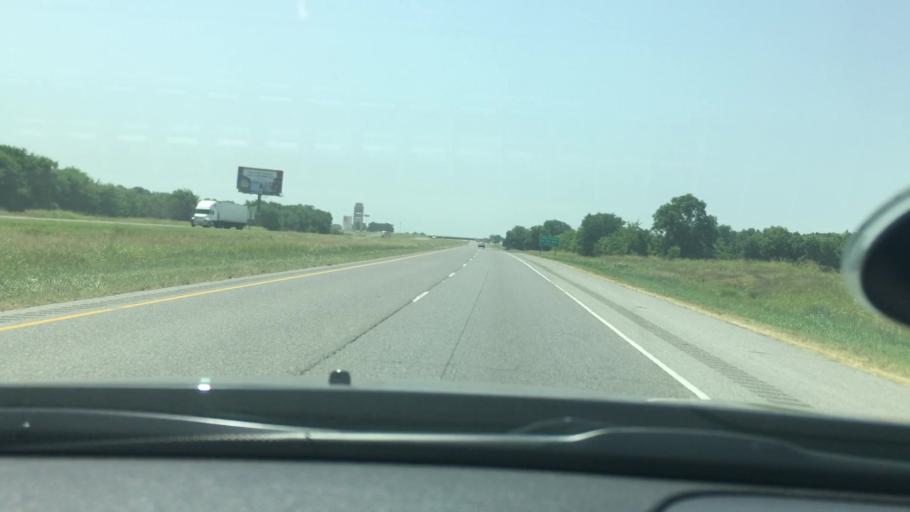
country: US
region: Oklahoma
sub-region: Murray County
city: Davis
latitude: 34.5161
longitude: -97.1810
